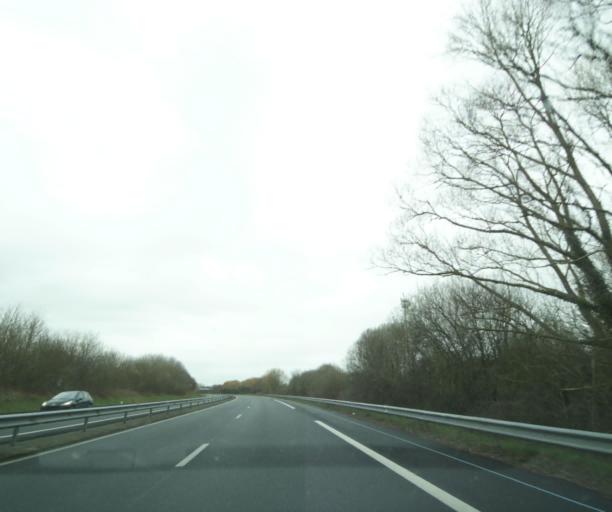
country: FR
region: Poitou-Charentes
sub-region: Departement de la Charente-Maritime
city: Tonnay-Charente
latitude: 45.9594
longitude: -0.8672
